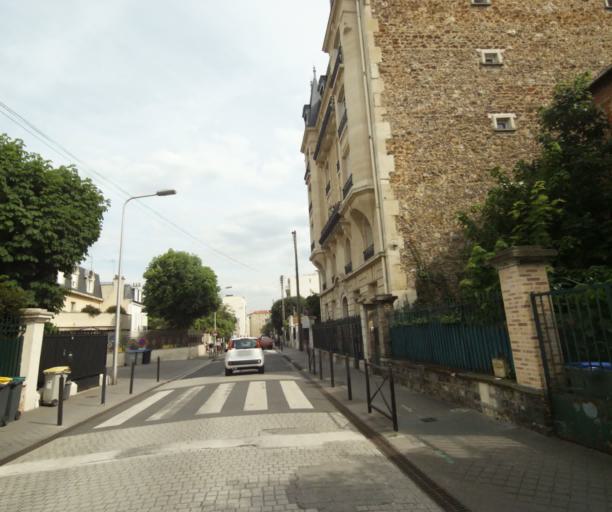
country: FR
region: Ile-de-France
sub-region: Departement des Hauts-de-Seine
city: Bois-Colombes
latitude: 48.9182
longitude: 2.2701
